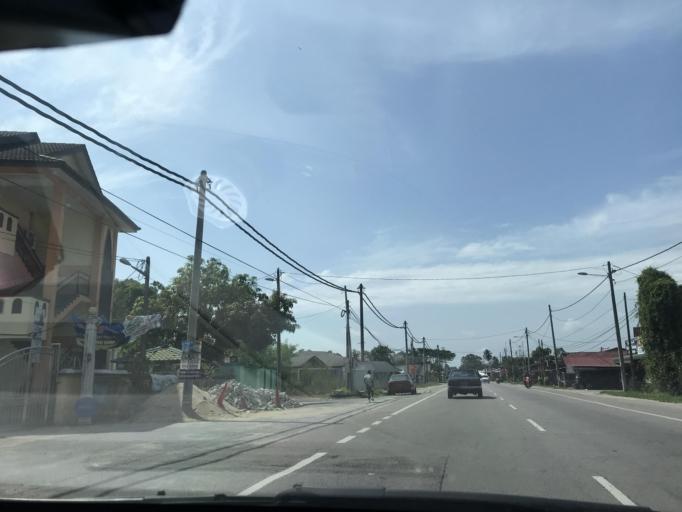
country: MY
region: Kelantan
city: Tumpat
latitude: 6.1513
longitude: 102.1585
